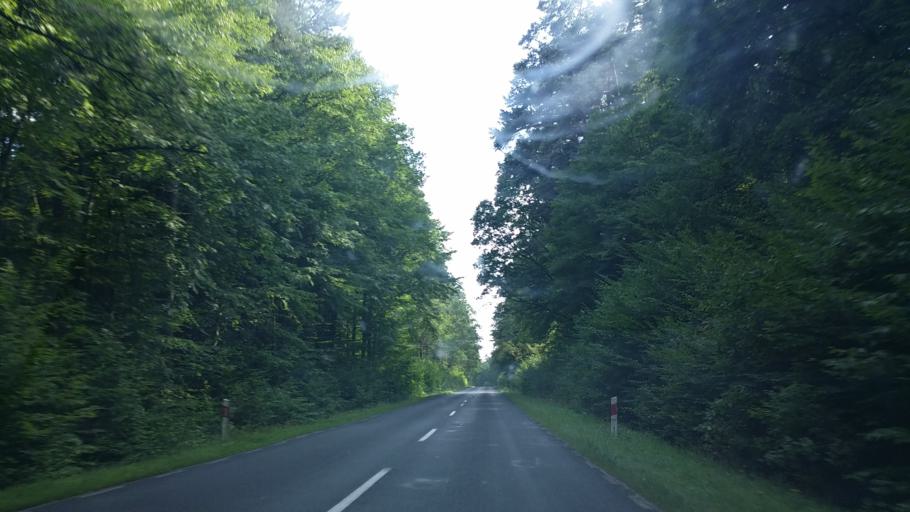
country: PL
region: Lubusz
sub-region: Powiat gorzowski
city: Klodawa
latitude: 52.8602
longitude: 15.2020
